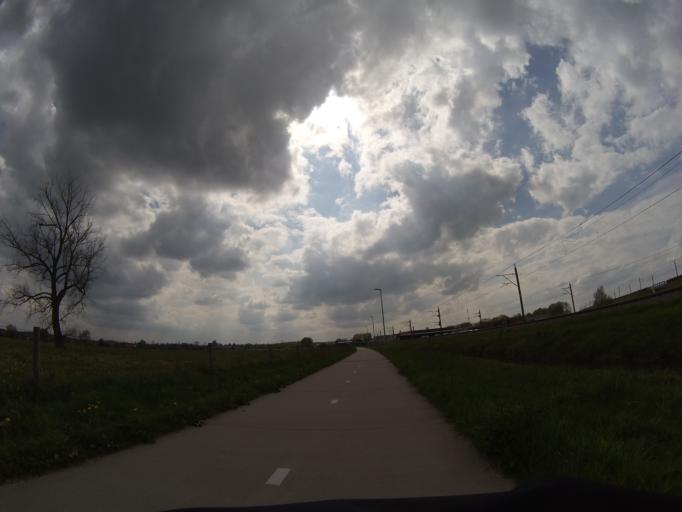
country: NL
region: Gelderland
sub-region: Gemeente Hattem
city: Hattem
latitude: 52.4864
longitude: 6.0481
